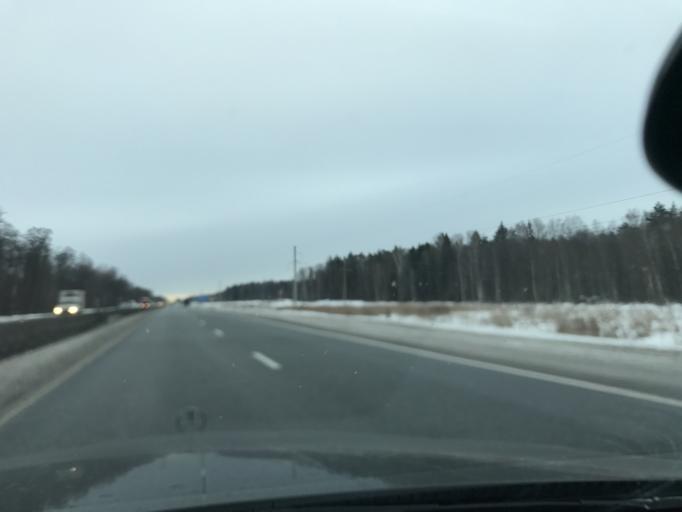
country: RU
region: Nizjnij Novgorod
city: Volodarsk
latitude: 56.2847
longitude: 43.1575
